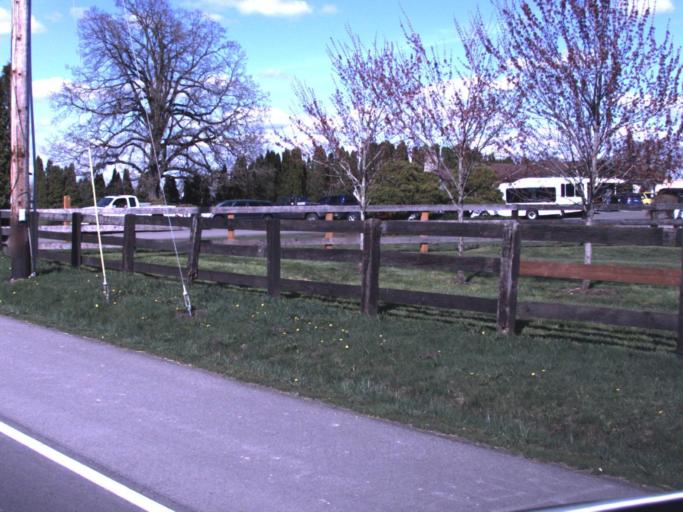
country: US
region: Washington
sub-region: King County
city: Lake Morton-Berrydale
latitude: 47.2391
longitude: -122.1095
